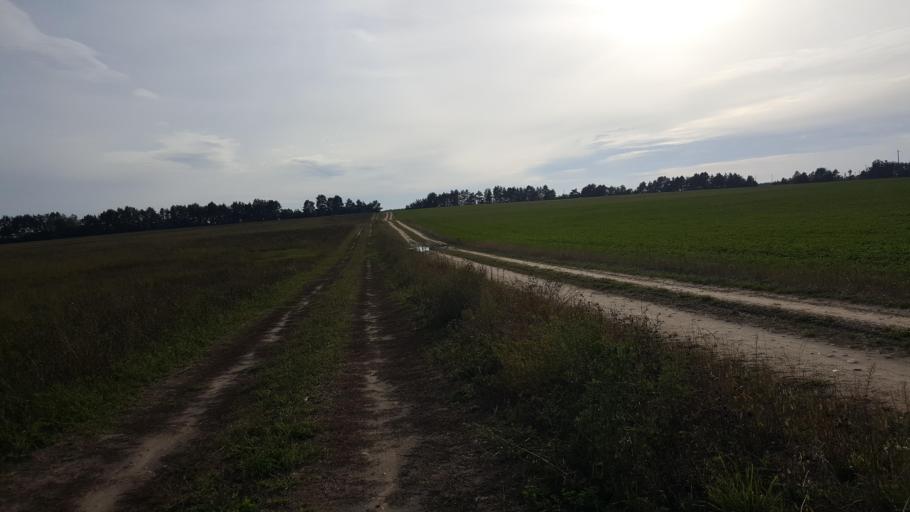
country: BY
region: Brest
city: Kamyanyets
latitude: 52.4021
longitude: 23.8585
